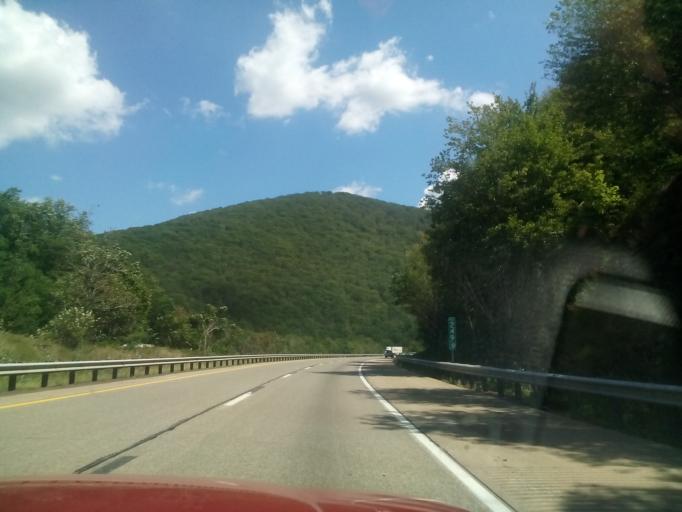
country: US
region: Pennsylvania
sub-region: Luzerne County
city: Nescopeck
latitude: 41.0191
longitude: -76.1745
